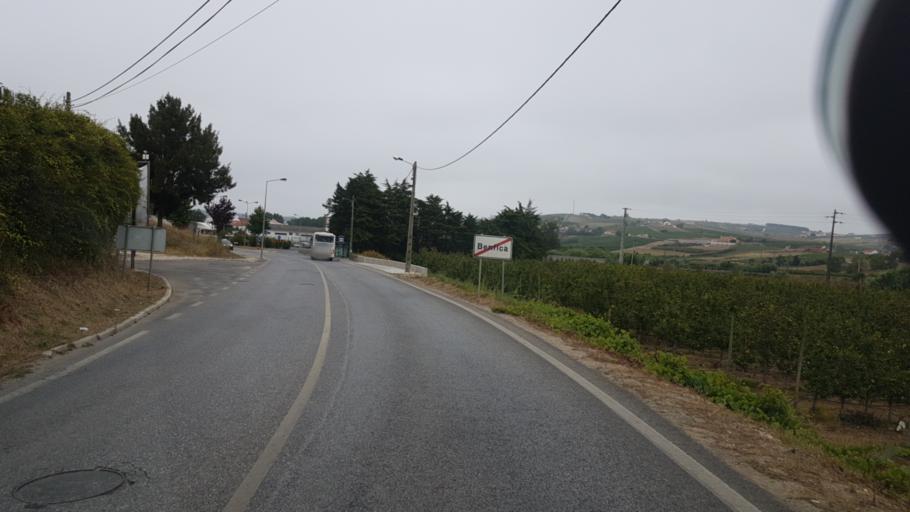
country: PT
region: Lisbon
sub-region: Torres Vedras
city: Torres Vedras
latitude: 39.0878
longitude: -9.3096
